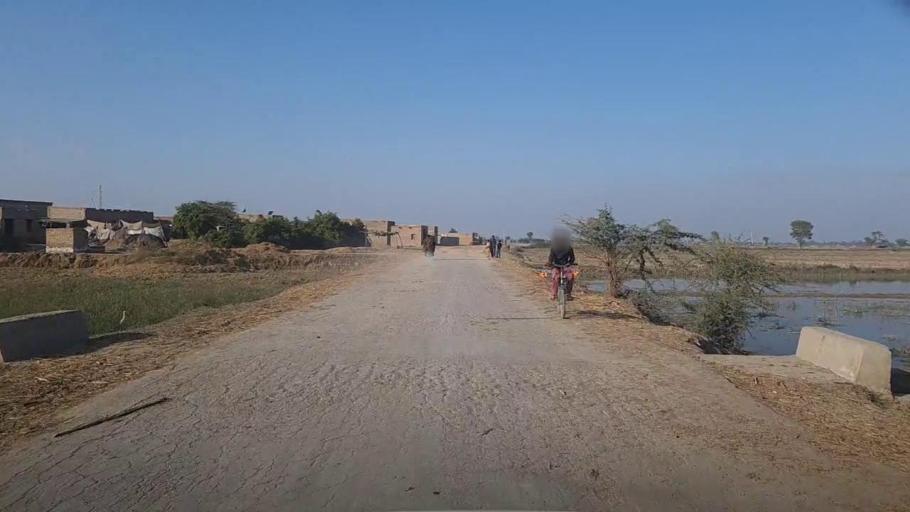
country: PK
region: Sindh
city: Phulji
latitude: 26.8665
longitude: 67.7931
